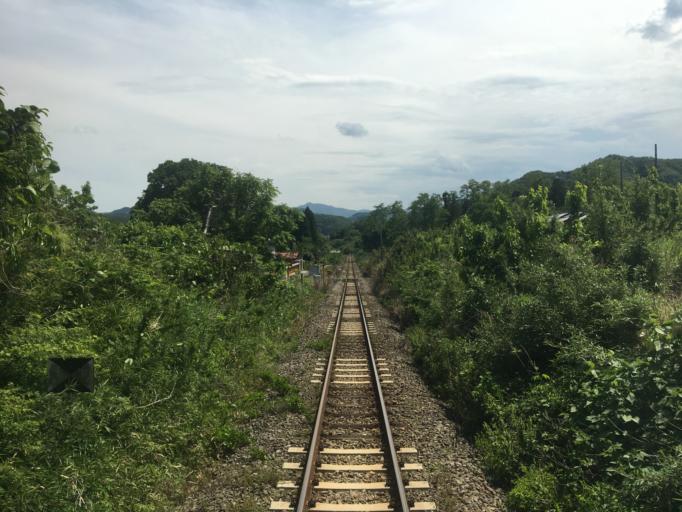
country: JP
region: Saitama
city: Yorii
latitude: 36.1042
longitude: 139.1931
